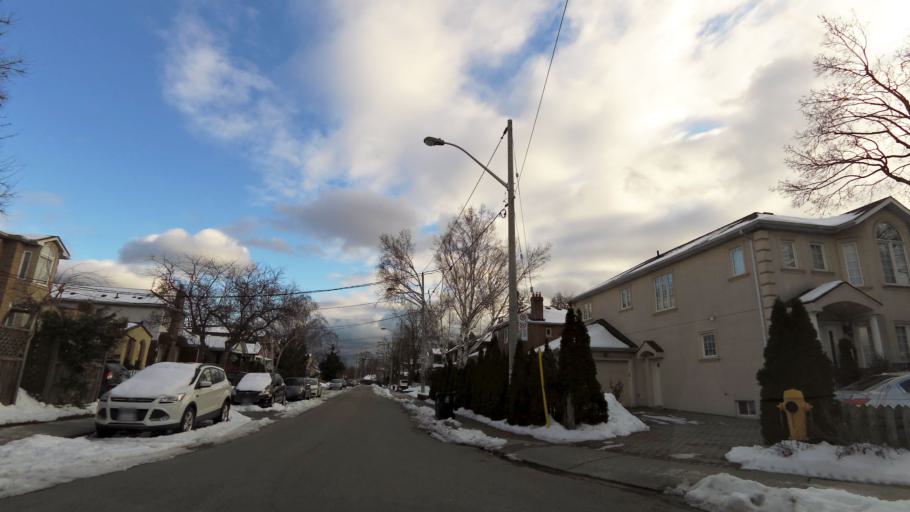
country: CA
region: Ontario
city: Toronto
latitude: 43.6956
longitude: -79.3524
